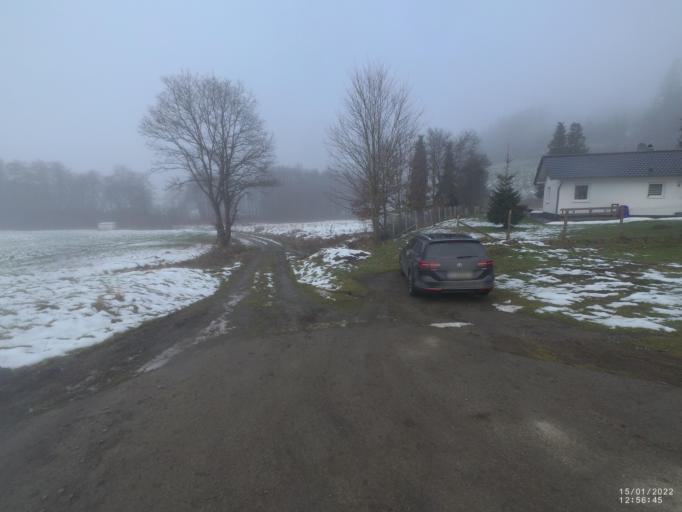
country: DE
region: North Rhine-Westphalia
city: Kierspe
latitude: 51.1105
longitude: 7.6097
